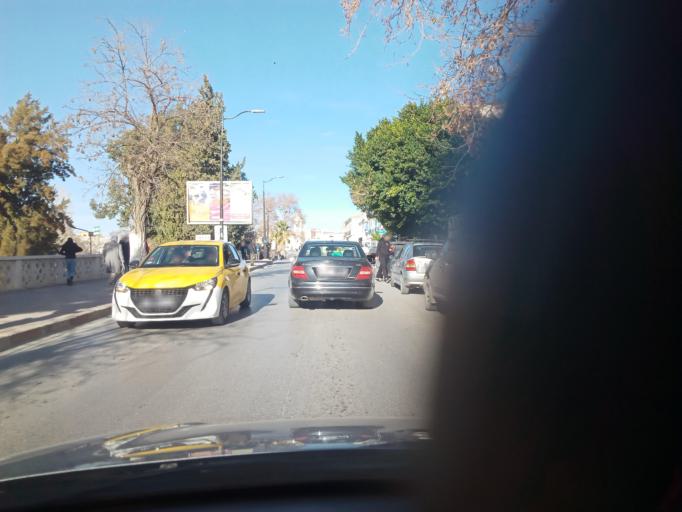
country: TN
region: Kef
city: El Kef
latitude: 36.1795
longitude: 8.7121
